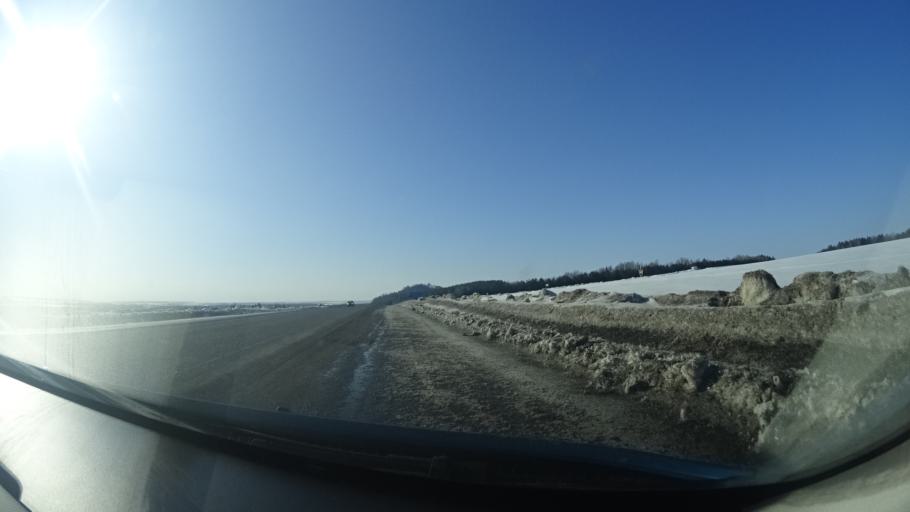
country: RU
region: Bashkortostan
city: Starobaltachevo
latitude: 56.0907
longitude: 55.9336
